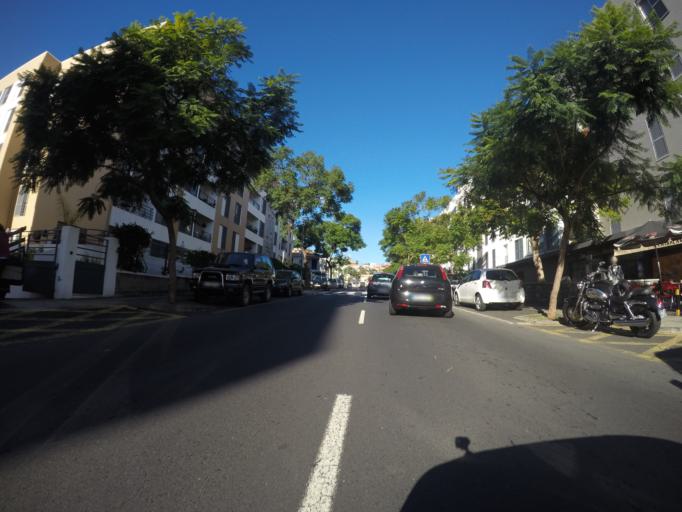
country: PT
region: Madeira
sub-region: Funchal
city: Nossa Senhora do Monte
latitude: 32.6611
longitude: -16.9316
